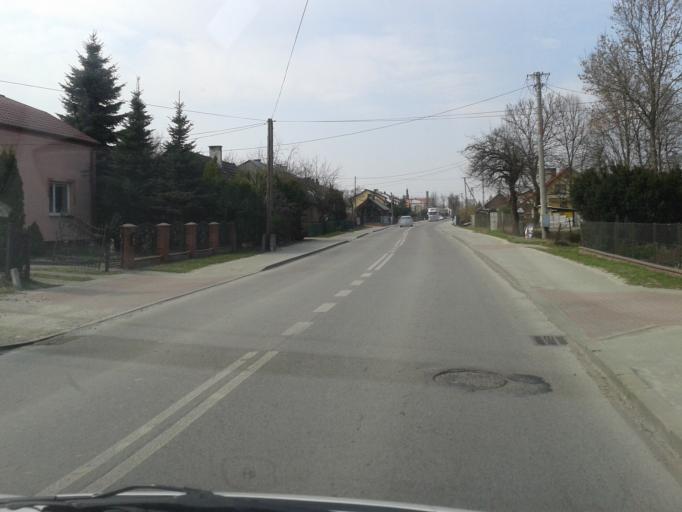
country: PL
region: Lublin Voivodeship
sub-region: Powiat tomaszowski
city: Belzec
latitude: 50.3840
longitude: 23.4343
